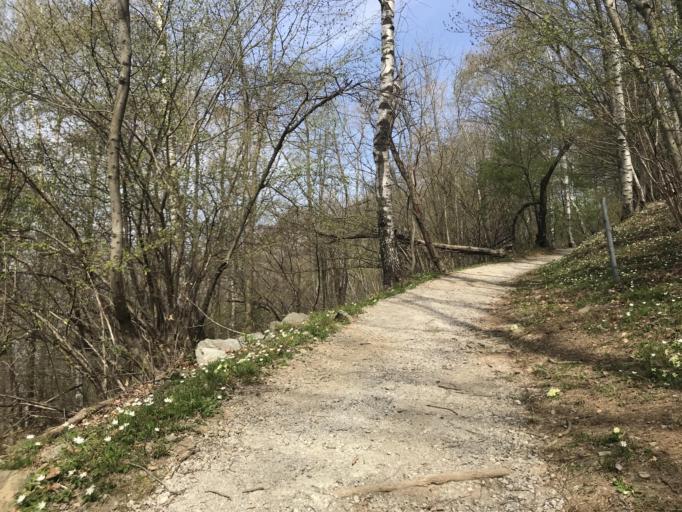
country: CH
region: Ticino
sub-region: Lugano District
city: Pregassona
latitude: 46.0091
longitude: 8.9841
